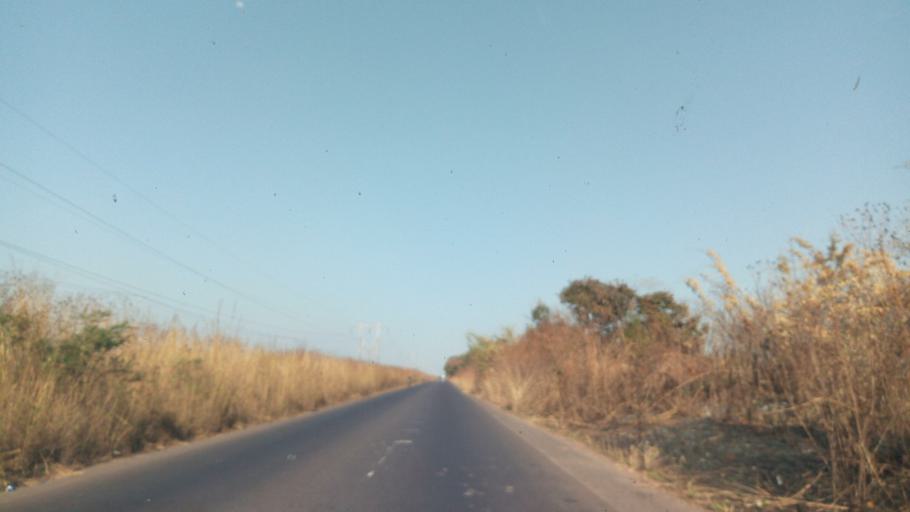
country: CD
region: Katanga
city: Likasi
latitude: -11.0029
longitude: 26.8980
